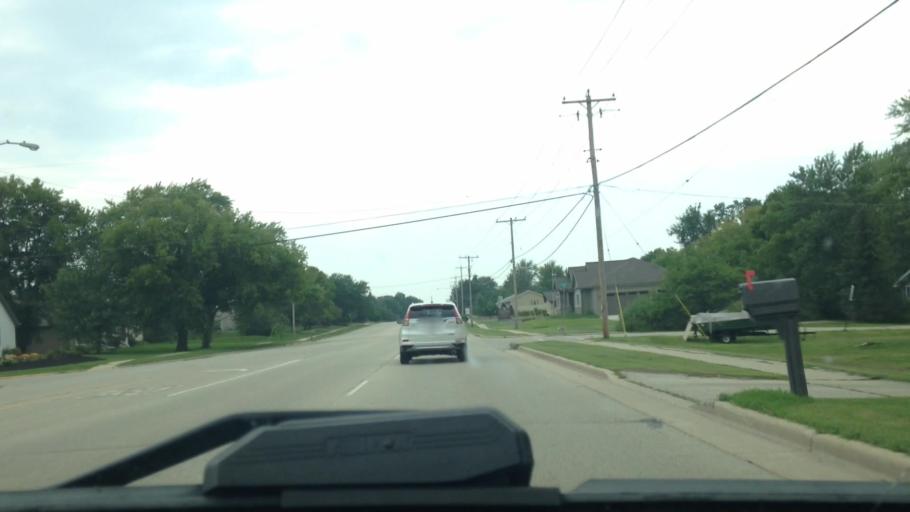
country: US
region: Wisconsin
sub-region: Waukesha County
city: Menomonee Falls
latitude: 43.1543
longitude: -88.1042
